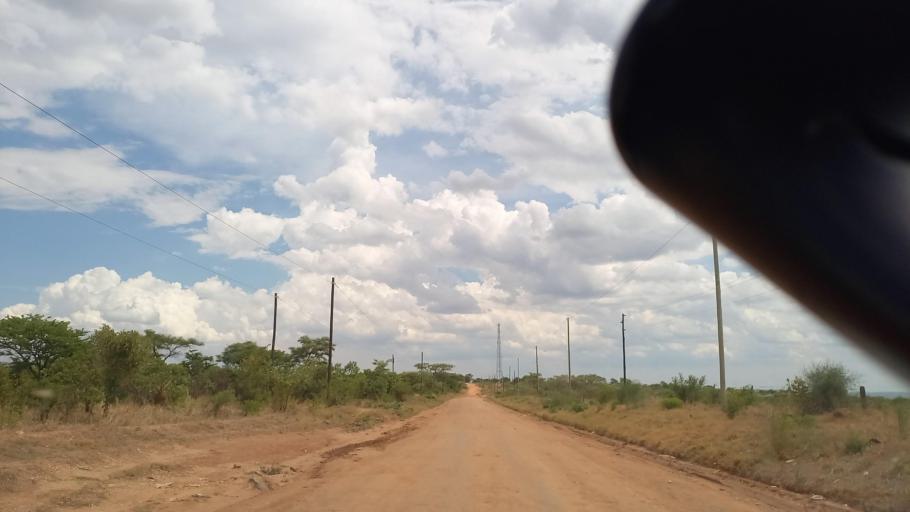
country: ZM
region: Southern
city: Nakambala
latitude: -16.0300
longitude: 27.9683
